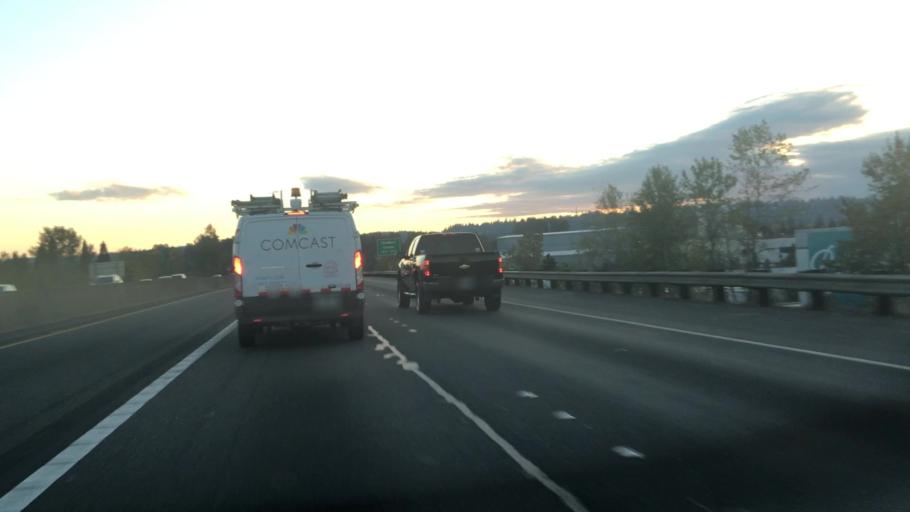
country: US
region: Washington
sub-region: King County
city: Kent
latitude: 47.3943
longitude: -122.2351
